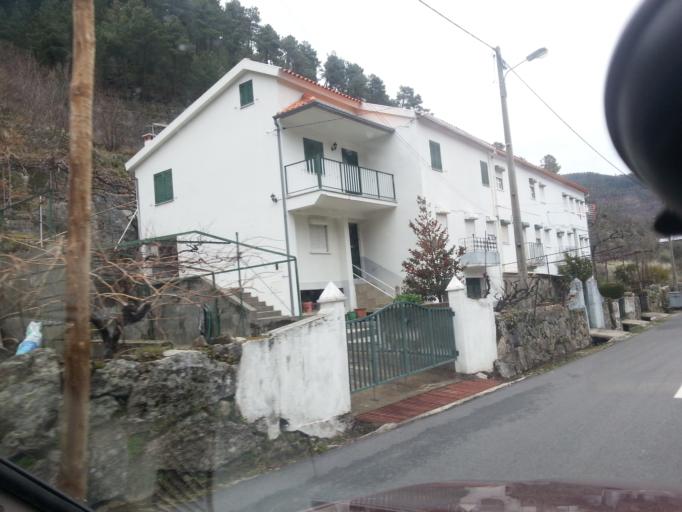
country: PT
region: Guarda
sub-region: Manteigas
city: Manteigas
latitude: 40.3898
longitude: -7.5447
